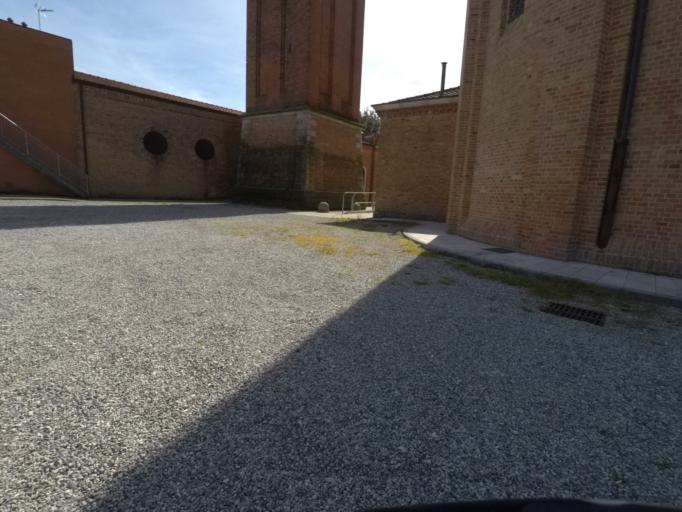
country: IT
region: Friuli Venezia Giulia
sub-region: Provincia di Pordenone
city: Orcenico Inferiore
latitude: 45.9424
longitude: 12.7540
